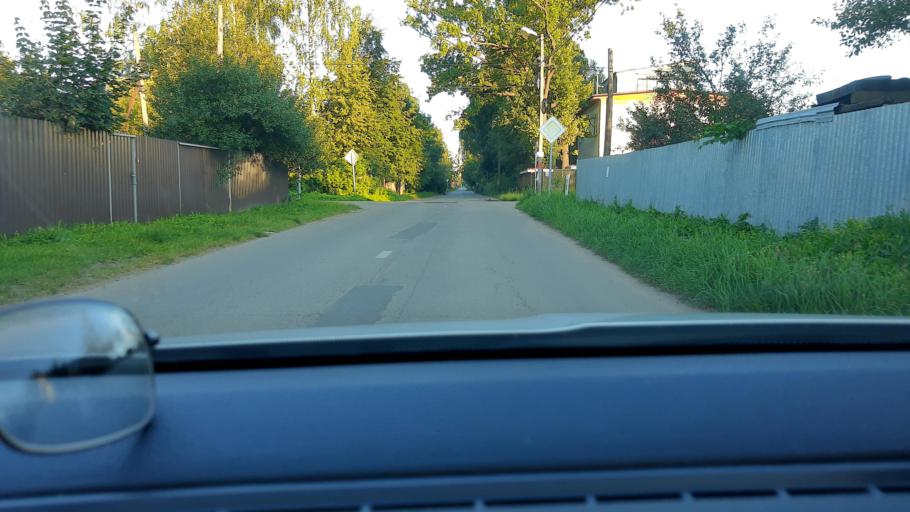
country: RU
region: Moskovskaya
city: Levoberezhnaya
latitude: 55.9191
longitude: 37.4754
